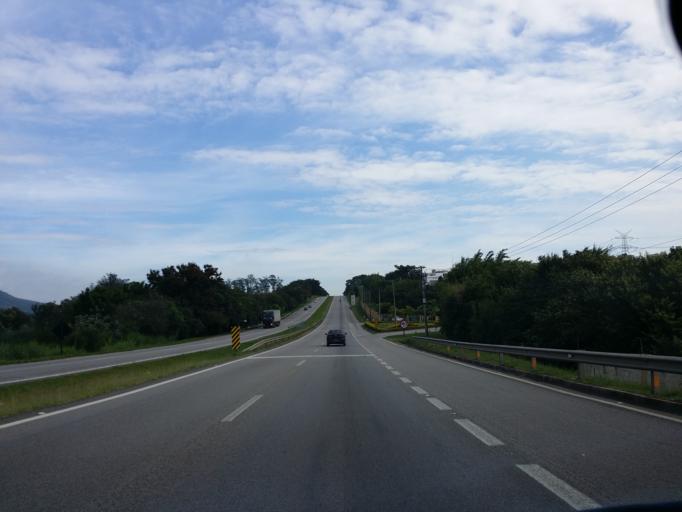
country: BR
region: Sao Paulo
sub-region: Itupeva
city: Itupeva
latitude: -23.2066
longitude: -47.0117
